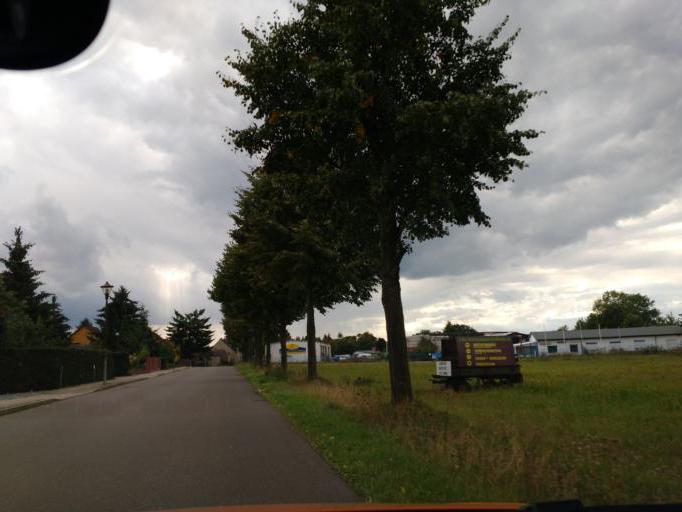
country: DE
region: Brandenburg
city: Reichenwalde
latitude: 52.2655
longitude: 14.0045
